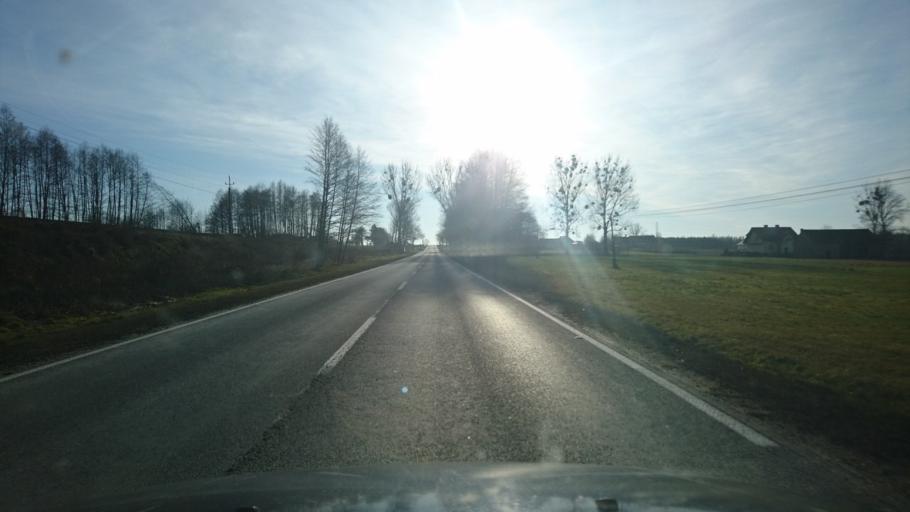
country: PL
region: Opole Voivodeship
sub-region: Powiat oleski
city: Dalachow
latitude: 51.0675
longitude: 18.6011
